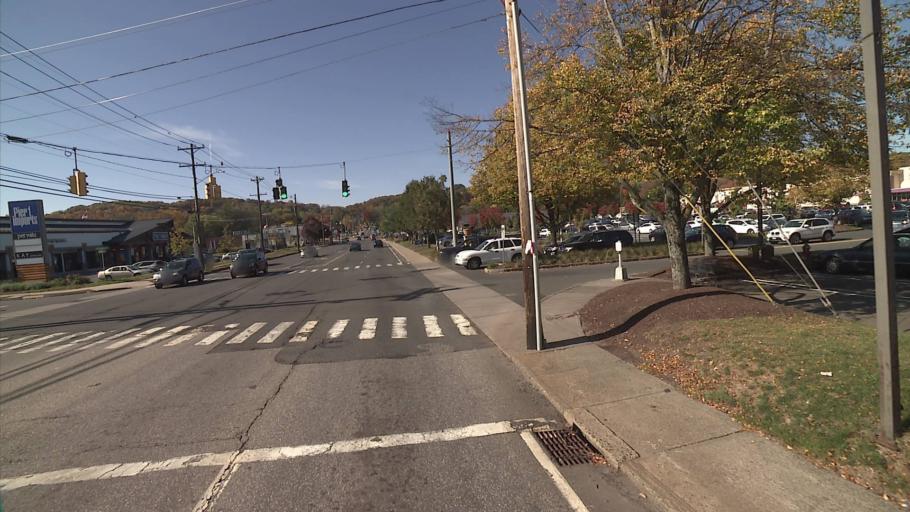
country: US
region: Connecticut
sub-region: Hartford County
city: Bristol
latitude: 41.6908
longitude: -72.9227
